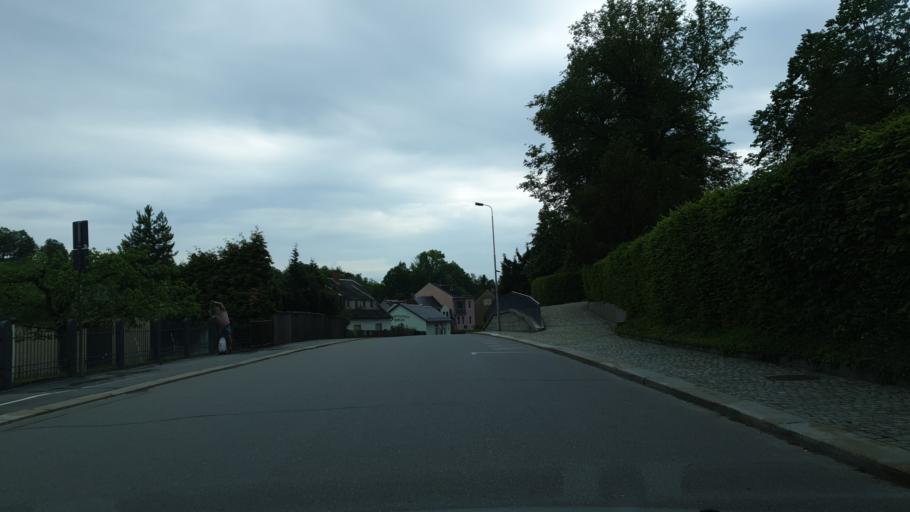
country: DE
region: Saxony
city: Stollberg
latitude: 50.7047
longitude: 12.7758
